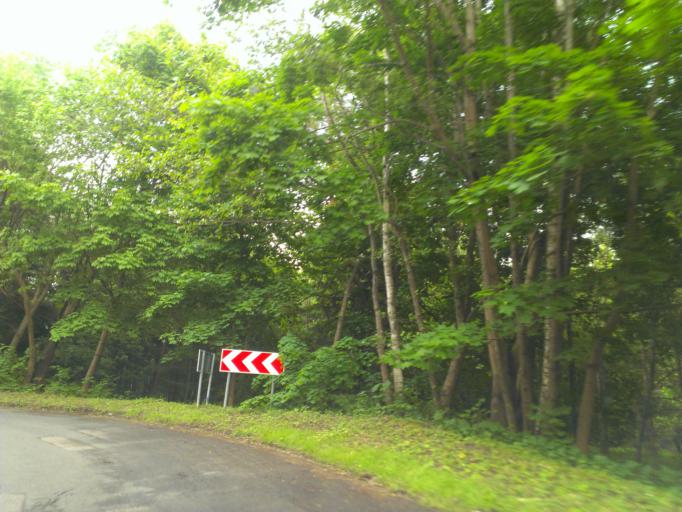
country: LT
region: Klaipedos apskritis
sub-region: Klaipeda
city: Klaipeda
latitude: 55.7666
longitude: 21.0905
